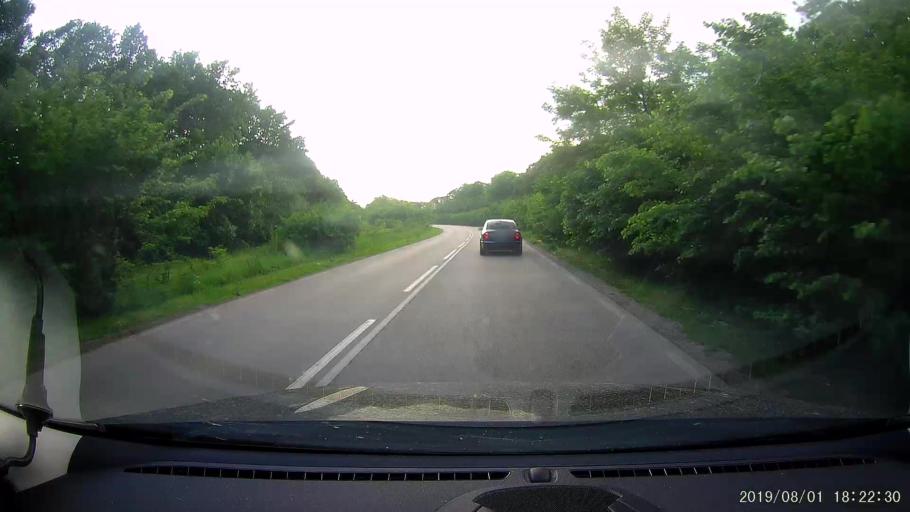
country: BG
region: Shumen
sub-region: Obshtina Kaolinovo
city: Kaolinovo
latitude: 43.6398
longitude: 27.0493
